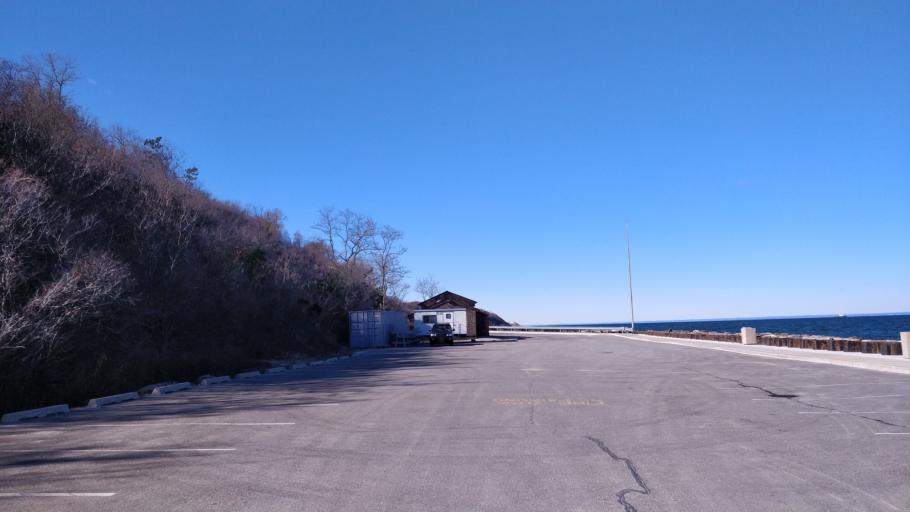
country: US
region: New York
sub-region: Suffolk County
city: Mount Sinai
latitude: 40.9638
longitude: -73.0483
